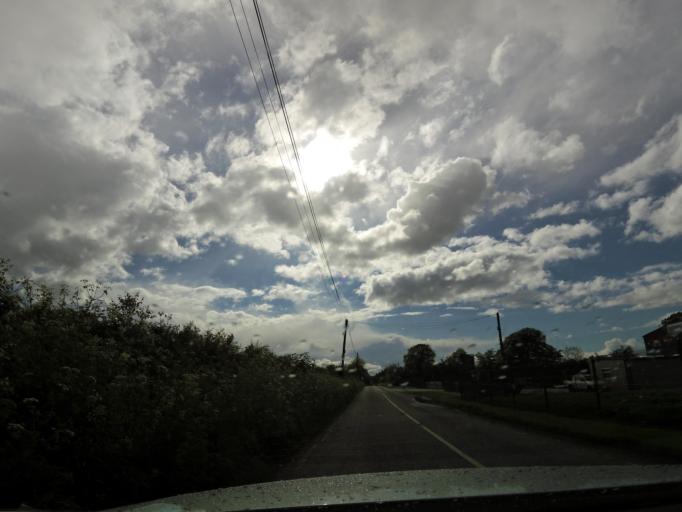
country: IE
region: Leinster
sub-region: Laois
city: Rathdowney
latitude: 52.7528
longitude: -7.6047
